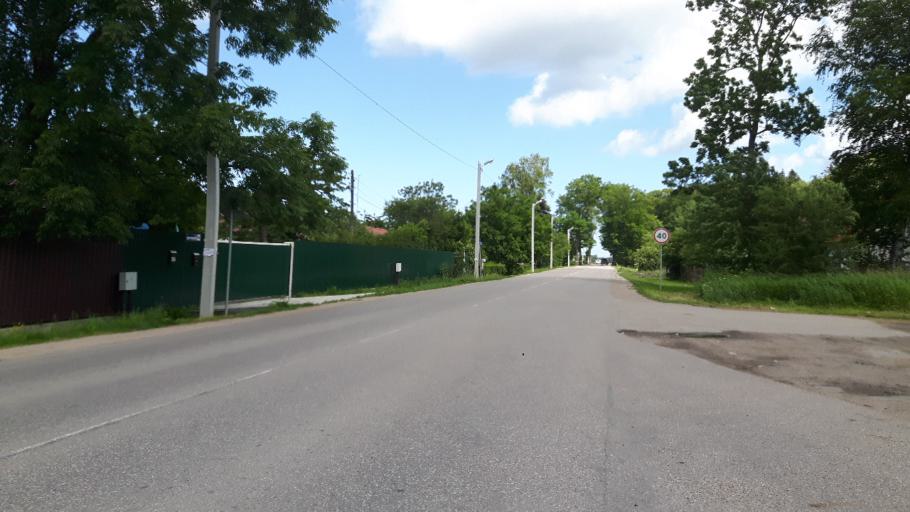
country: RU
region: Kaliningrad
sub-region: Zelenogradskiy Rayon
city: Zelenogradsk
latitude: 54.9387
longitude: 20.4509
